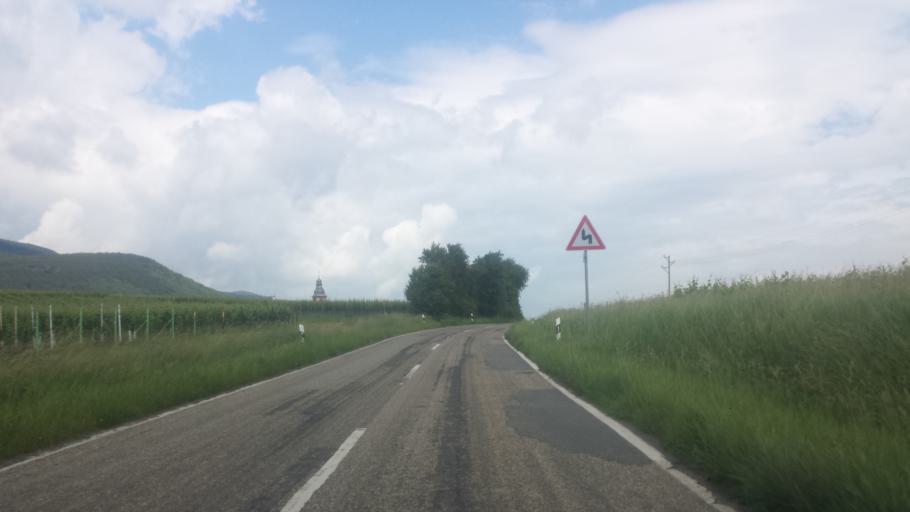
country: DE
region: Rheinland-Pfalz
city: Frankweiler
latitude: 49.2234
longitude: 8.0562
